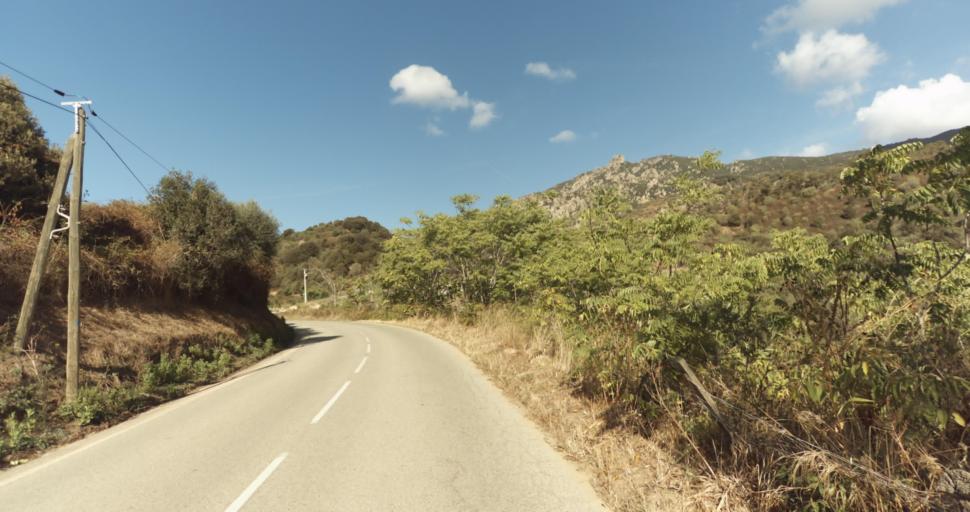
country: FR
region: Corsica
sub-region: Departement de la Corse-du-Sud
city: Ajaccio
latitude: 41.9298
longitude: 8.6961
